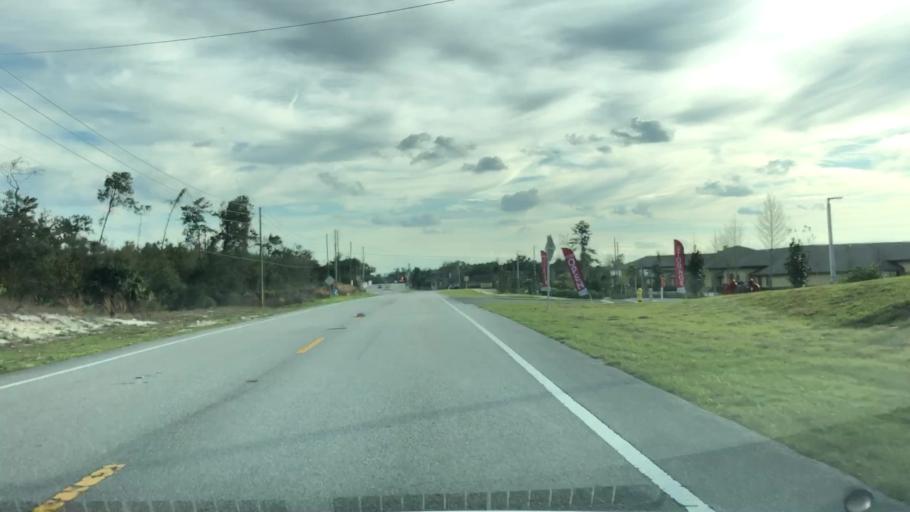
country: US
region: Florida
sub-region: Volusia County
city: Deltona
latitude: 28.9323
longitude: -81.2611
